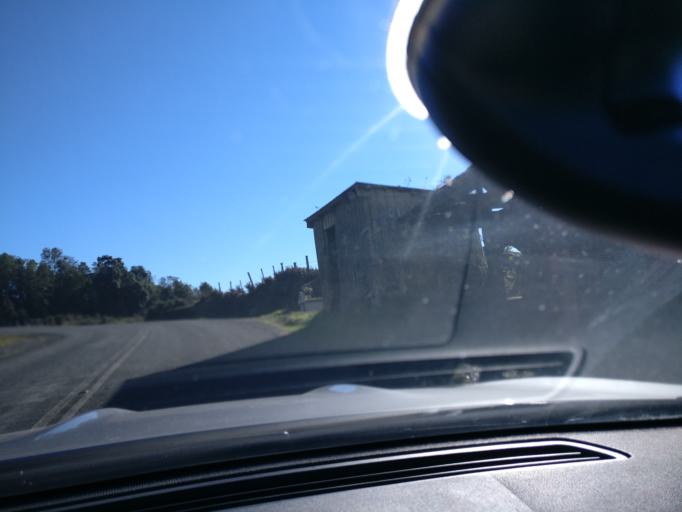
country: CL
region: Los Lagos
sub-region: Provincia de Chiloe
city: Castro
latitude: -42.3202
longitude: -73.3694
